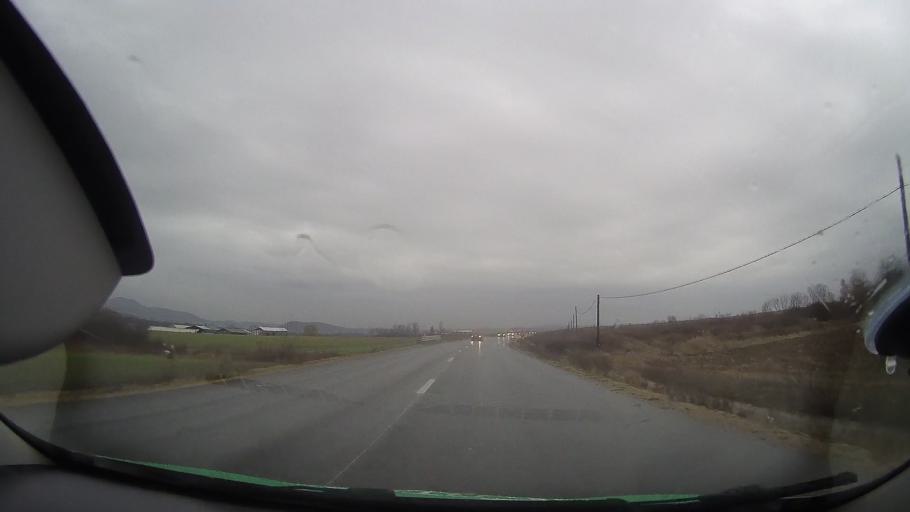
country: RO
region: Bihor
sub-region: Municipiul Beius
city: Beius
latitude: 46.6740
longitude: 22.3256
